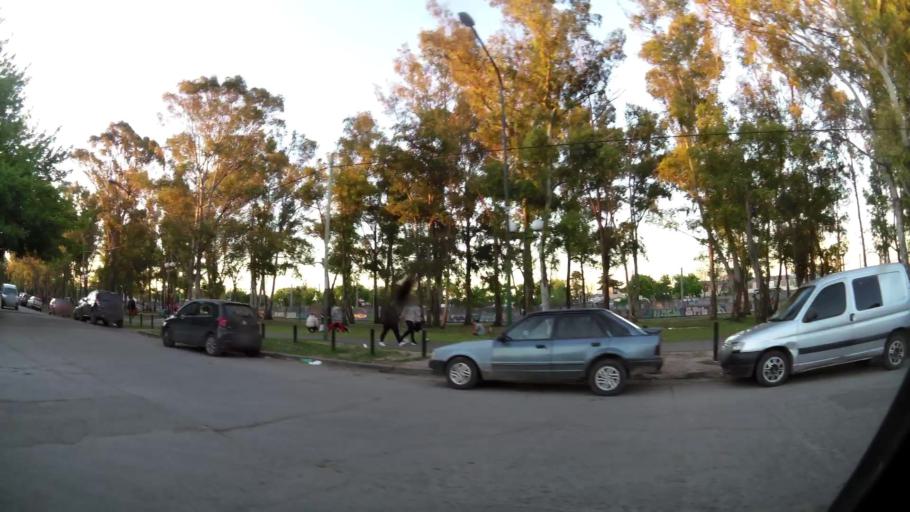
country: AR
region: Buenos Aires
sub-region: Partido de Almirante Brown
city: Adrogue
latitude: -34.8014
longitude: -58.3401
